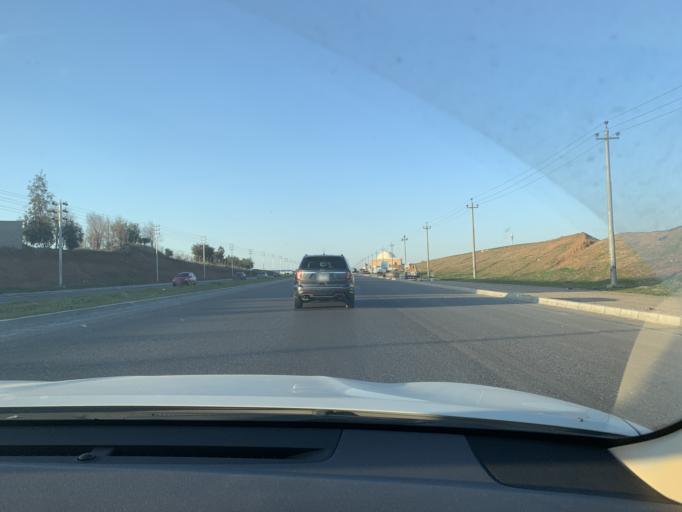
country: IQ
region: Arbil
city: Erbil
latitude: 36.2757
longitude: 44.0153
